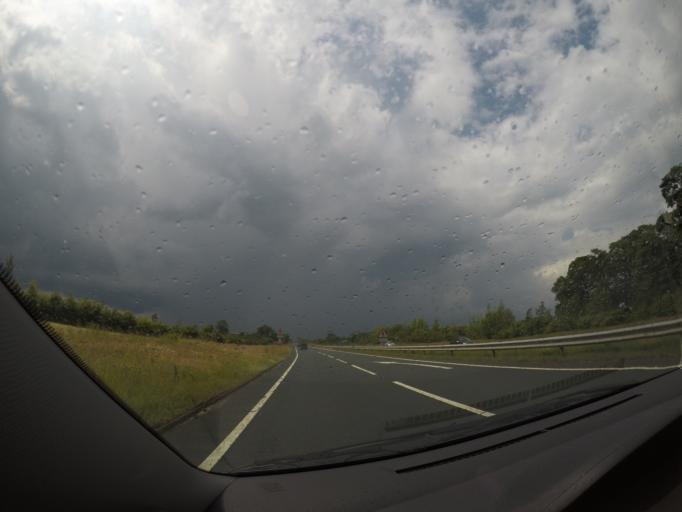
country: GB
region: England
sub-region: Cumbria
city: Penrith
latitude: 54.6507
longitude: -2.6325
